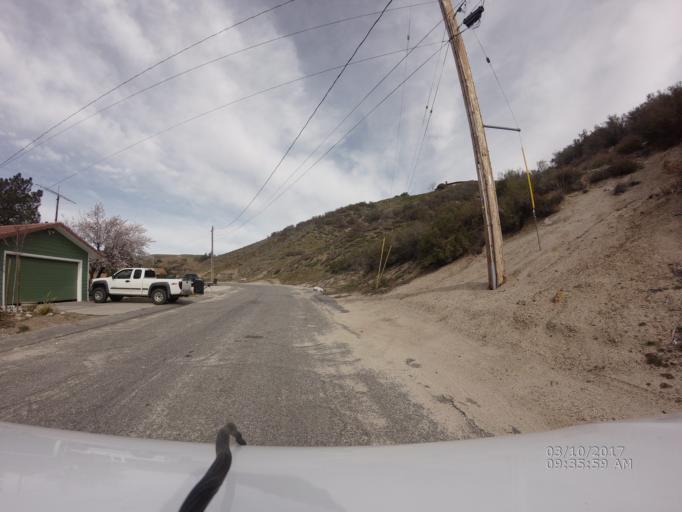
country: US
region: California
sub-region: Los Angeles County
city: Green Valley
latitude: 34.6656
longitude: -118.3871
